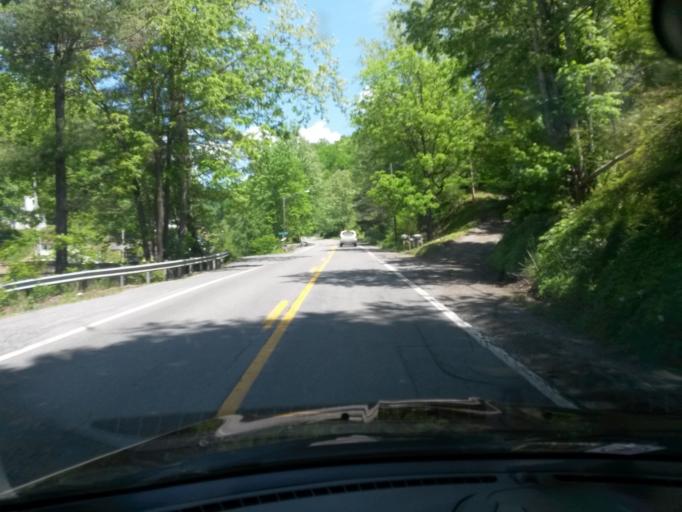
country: US
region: West Virginia
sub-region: McDowell County
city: Welch
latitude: 37.4713
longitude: -81.5417
